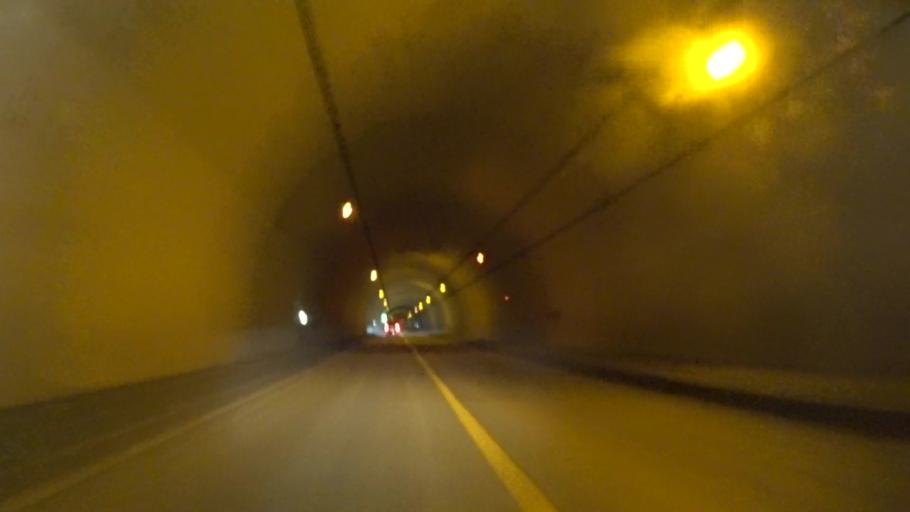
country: JP
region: Kyoto
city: Fukuchiyama
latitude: 35.4017
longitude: 135.0382
